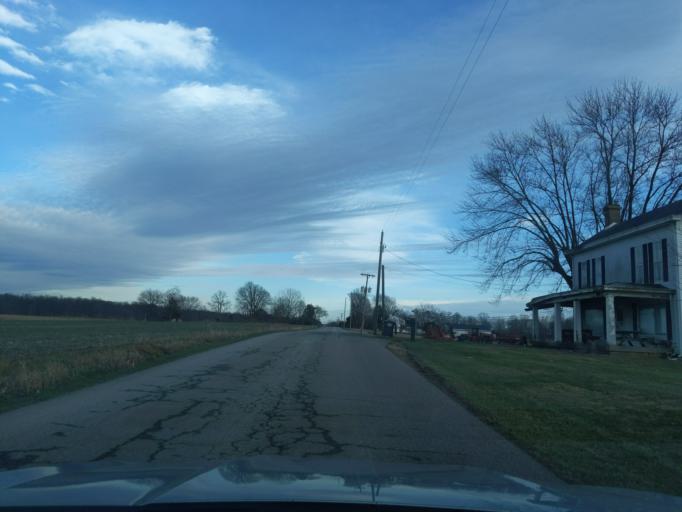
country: US
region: Indiana
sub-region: Decatur County
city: Westport
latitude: 39.2342
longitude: -85.5484
